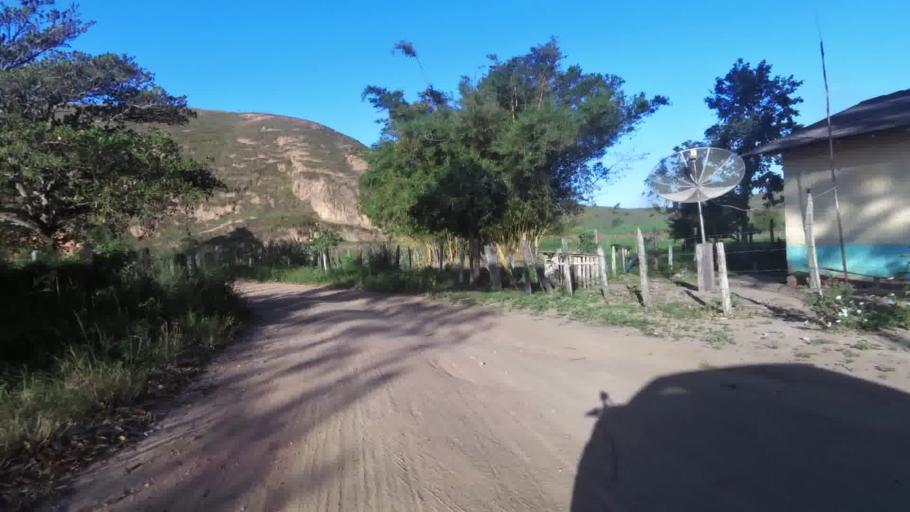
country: BR
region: Espirito Santo
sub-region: Marataizes
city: Marataizes
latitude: -21.1409
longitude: -41.0190
